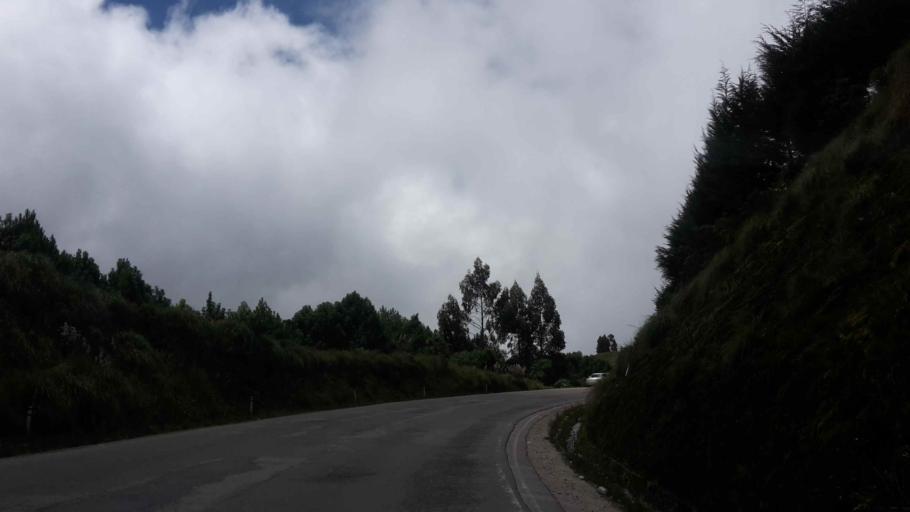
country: BO
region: Cochabamba
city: Colomi
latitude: -17.2517
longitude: -65.8961
